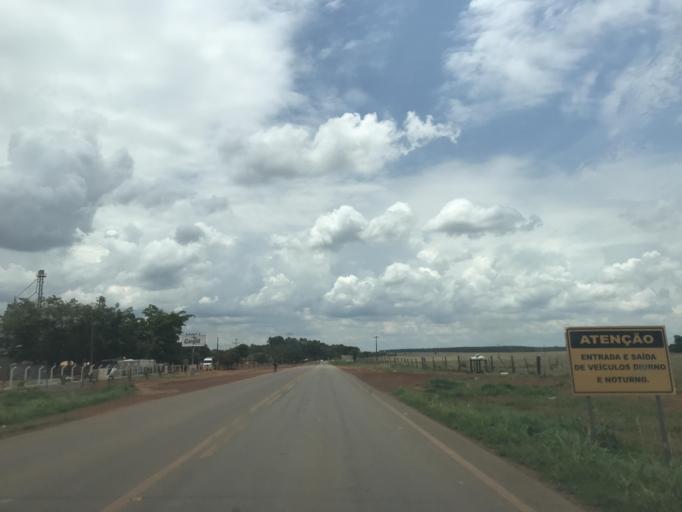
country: BR
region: Goias
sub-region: Vianopolis
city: Vianopolis
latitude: -16.7429
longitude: -48.4676
